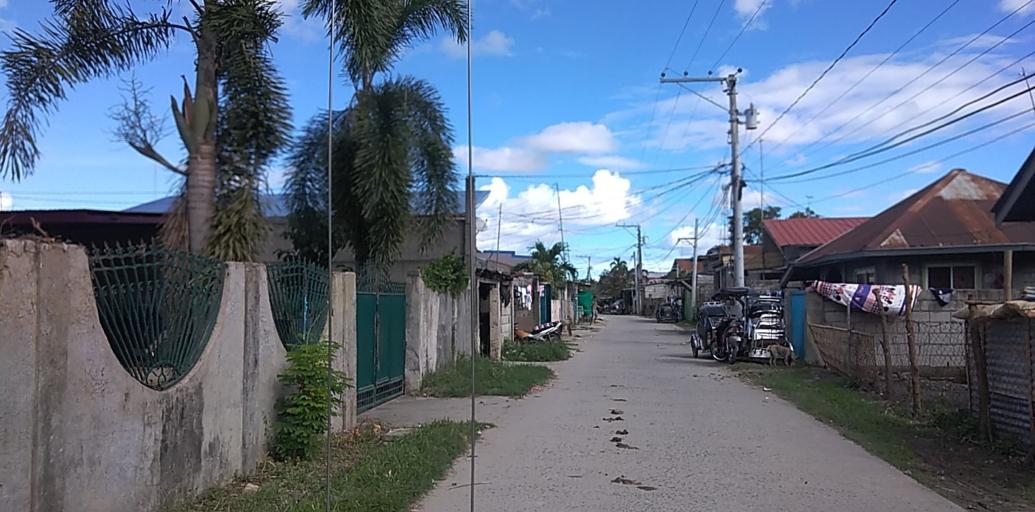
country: PH
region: Central Luzon
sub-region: Province of Pampanga
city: Candating
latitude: 15.1363
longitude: 120.7975
